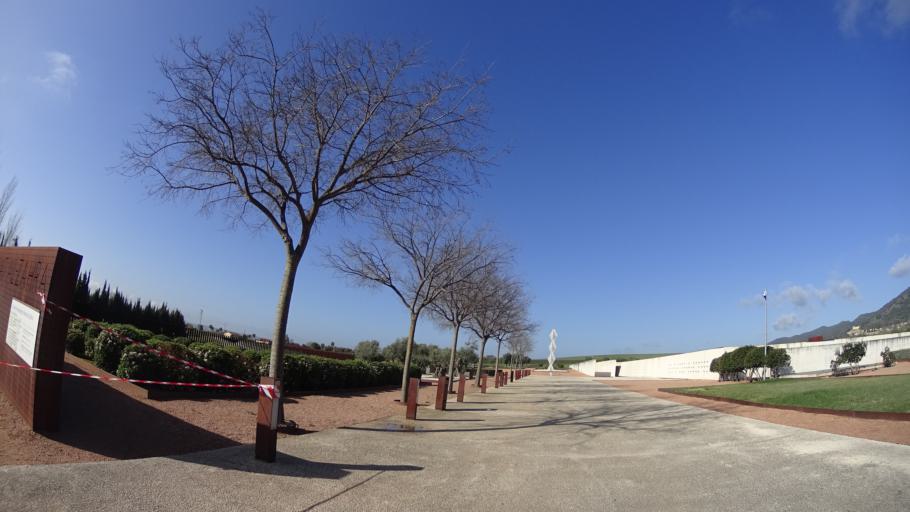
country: ES
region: Andalusia
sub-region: Province of Cordoba
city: Villarrubia
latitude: 37.8807
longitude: -4.8531
